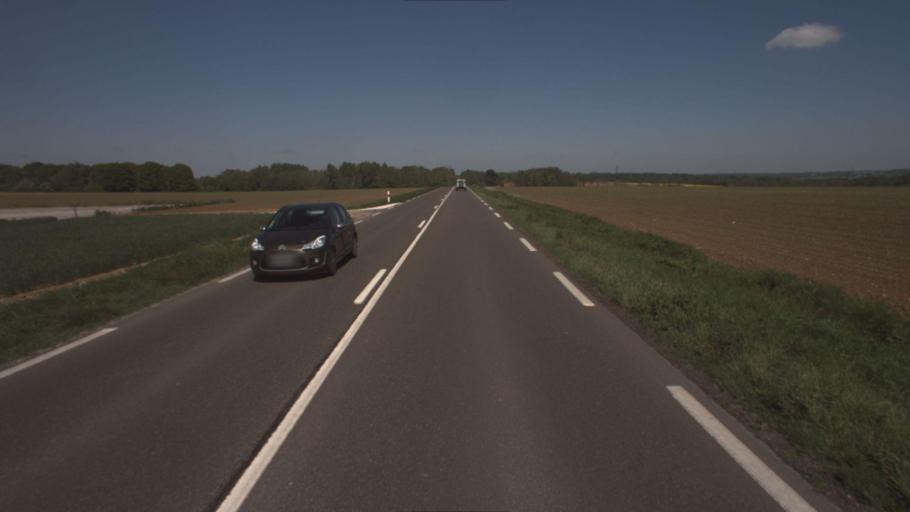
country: FR
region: Ile-de-France
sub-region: Departement de Seine-et-Marne
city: Villiers-sur-Morin
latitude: 48.8408
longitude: 2.8720
